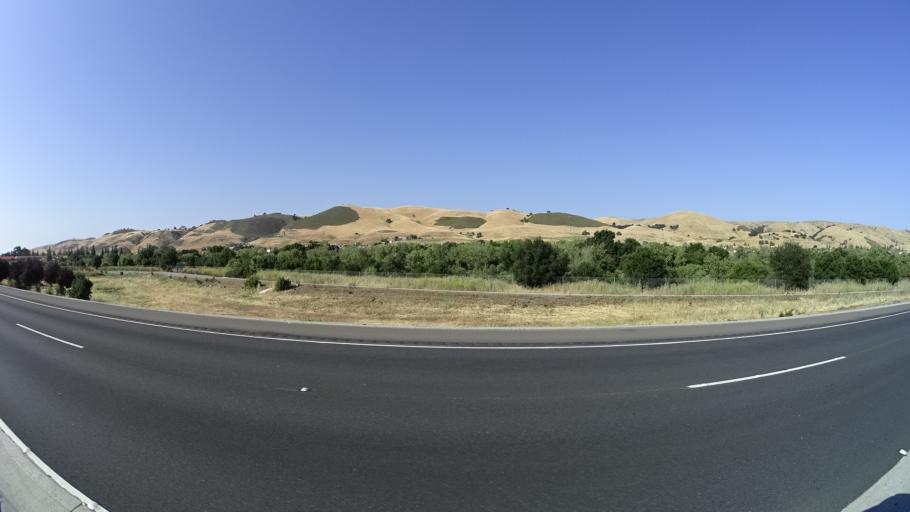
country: US
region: California
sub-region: Santa Clara County
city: Seven Trees
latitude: 37.2431
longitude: -121.7708
